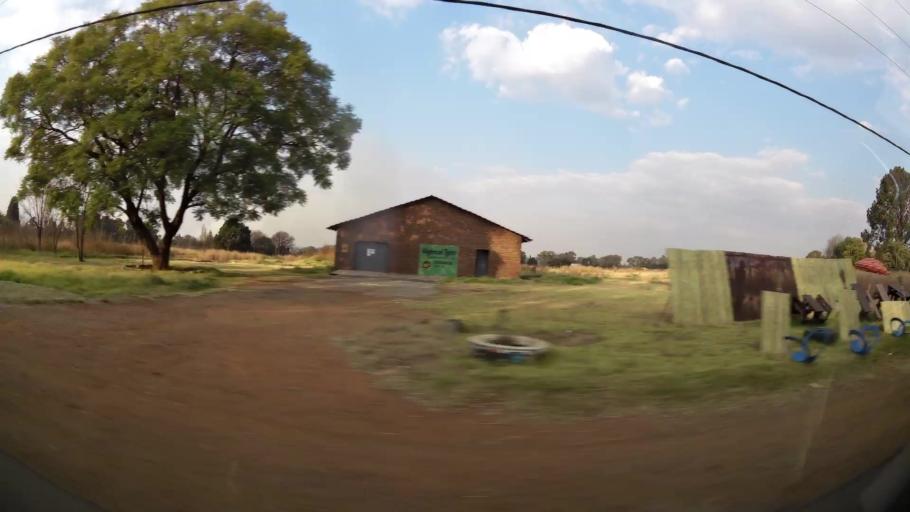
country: ZA
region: Gauteng
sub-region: Ekurhuleni Metropolitan Municipality
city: Benoni
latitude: -26.1247
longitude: 28.2937
